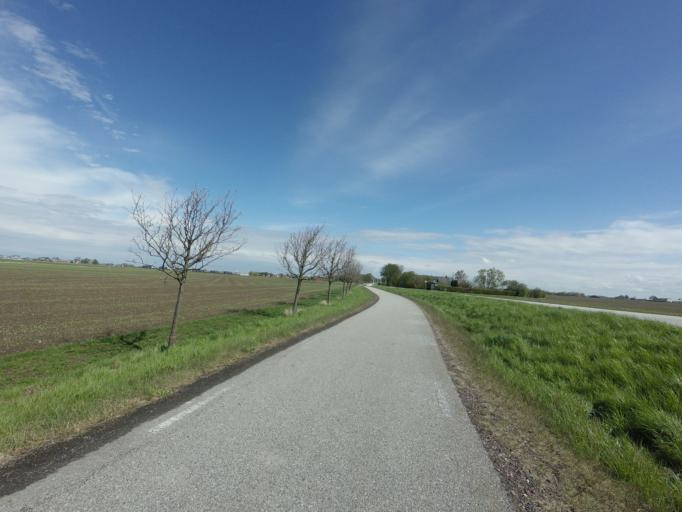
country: SE
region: Skane
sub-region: Malmo
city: Tygelsjo
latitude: 55.5084
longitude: 12.9930
